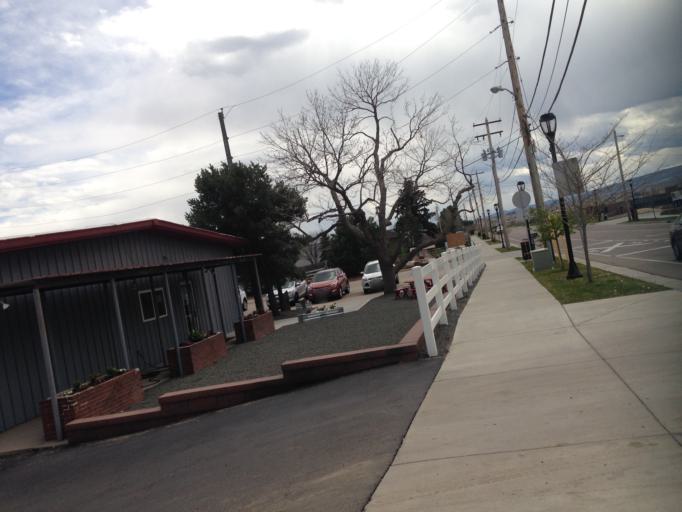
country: US
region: Colorado
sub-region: Jefferson County
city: Applewood
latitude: 39.7884
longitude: -105.1308
